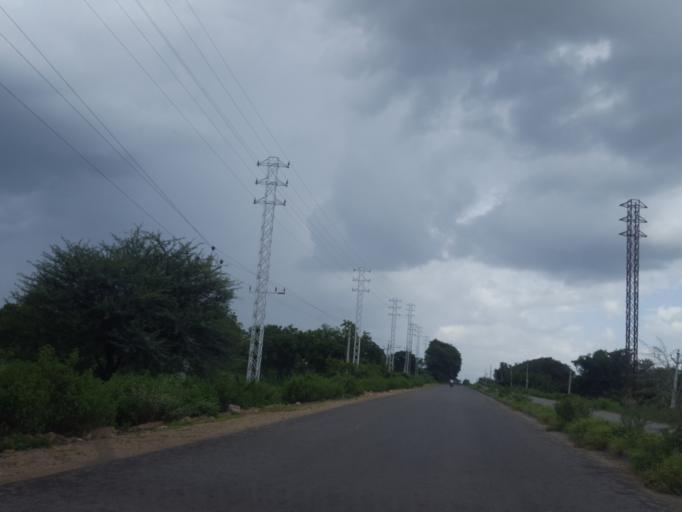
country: IN
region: Telangana
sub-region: Medak
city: Serilingampalle
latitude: 17.4114
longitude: 78.2701
